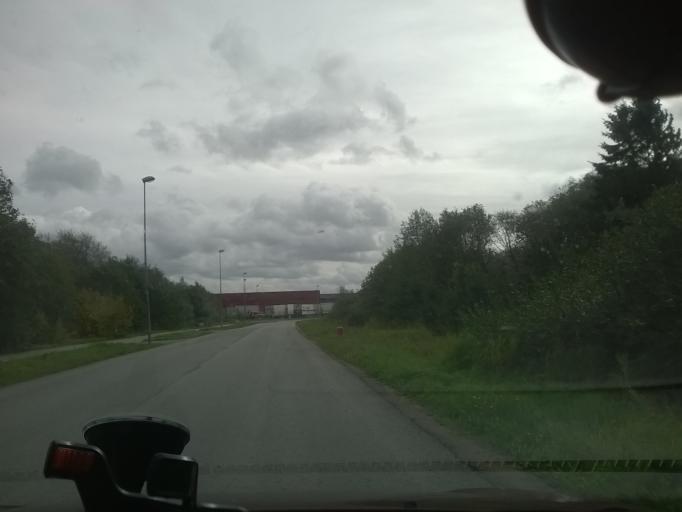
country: EE
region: Harju
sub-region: Rae vald
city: Jueri
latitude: 59.3853
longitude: 24.8303
